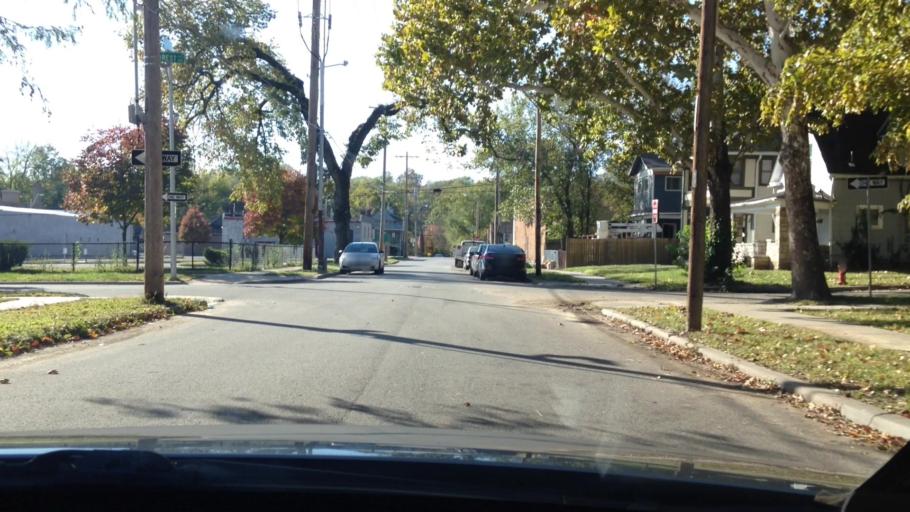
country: US
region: Kansas
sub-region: Johnson County
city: Westwood
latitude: 39.0453
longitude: -94.5711
